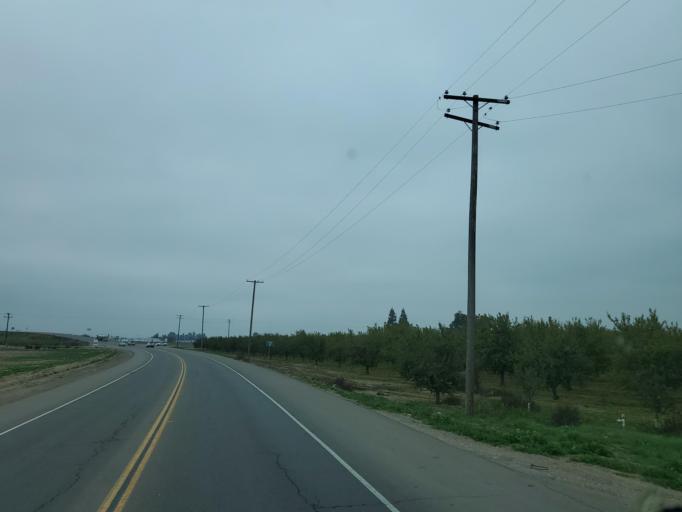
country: US
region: California
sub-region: Stanislaus County
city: Keyes
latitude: 37.5478
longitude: -120.9139
